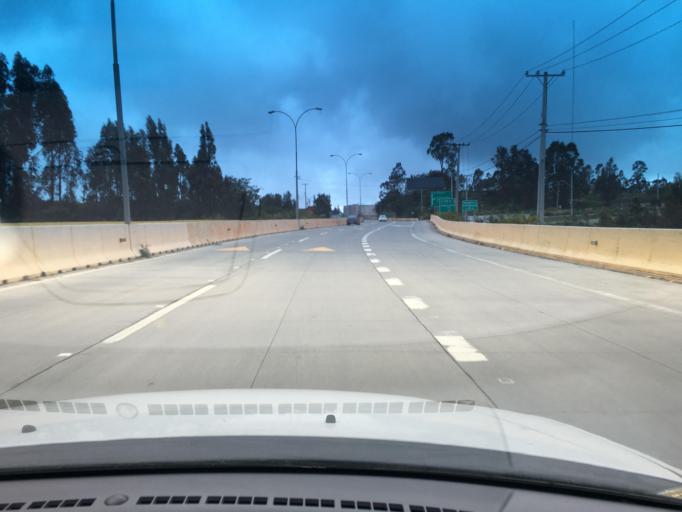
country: CL
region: Valparaiso
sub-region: Provincia de Valparaiso
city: Valparaiso
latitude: -33.0712
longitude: -71.6287
